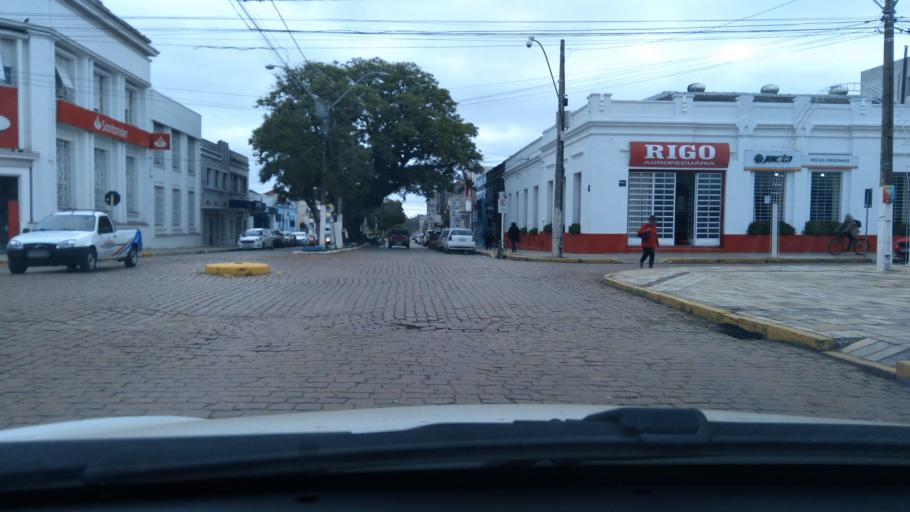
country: BR
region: Rio Grande do Sul
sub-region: Dom Pedrito
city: Dom Pedrito
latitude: -30.9845
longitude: -54.6752
